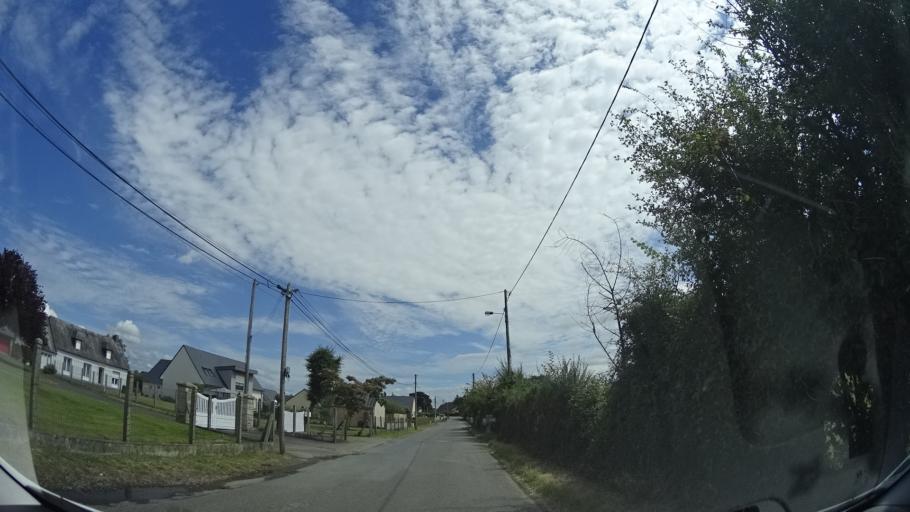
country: FR
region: Lower Normandy
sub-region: Departement de la Manche
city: Sartilly
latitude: 48.6872
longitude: -1.4833
